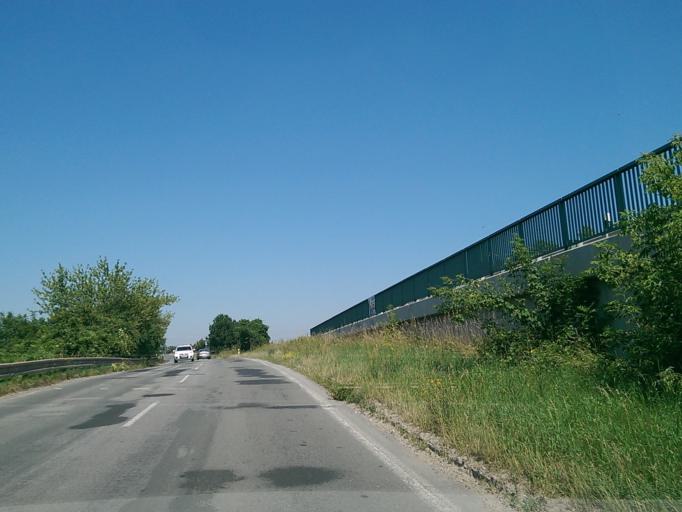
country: CZ
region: Central Bohemia
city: Benatky nad Jizerou
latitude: 50.2946
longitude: 14.8480
